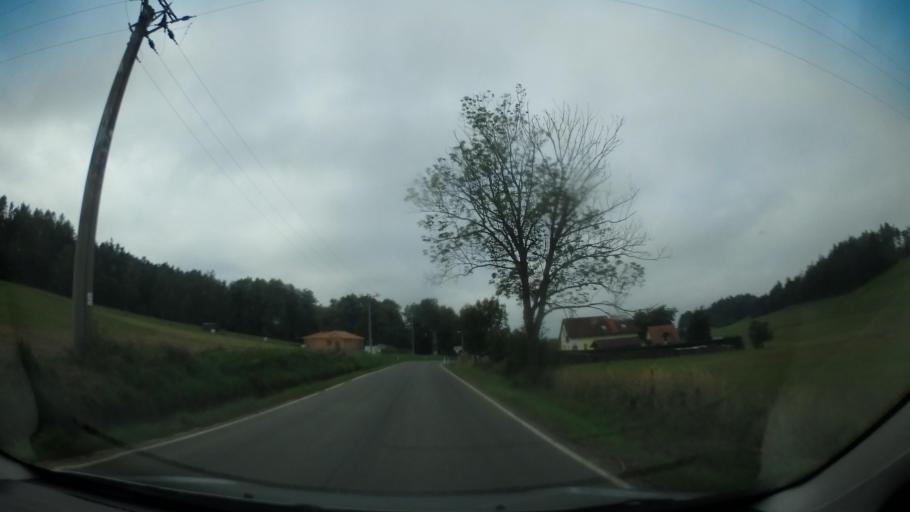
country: CZ
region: Central Bohemia
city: Neveklov
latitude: 49.7244
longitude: 14.4866
